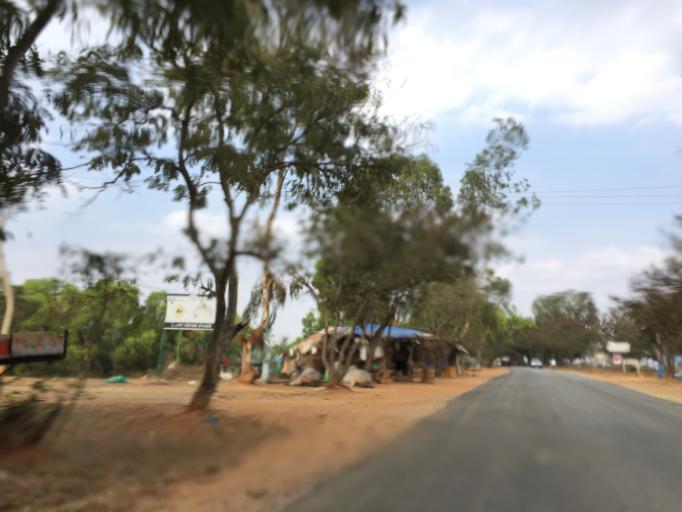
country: IN
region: Karnataka
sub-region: Chikkaballapur
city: Chik Ballapur
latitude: 13.3966
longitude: 77.7041
